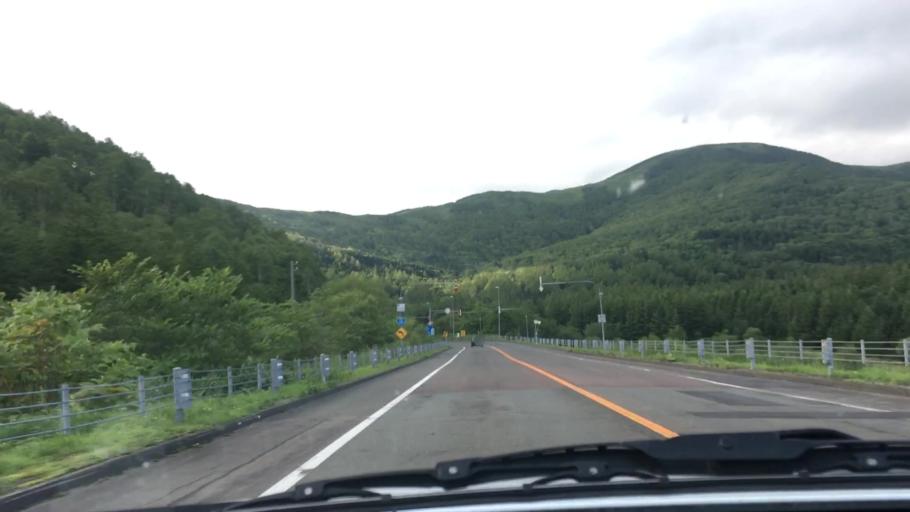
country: JP
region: Hokkaido
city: Shimo-furano
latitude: 43.1364
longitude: 142.7544
